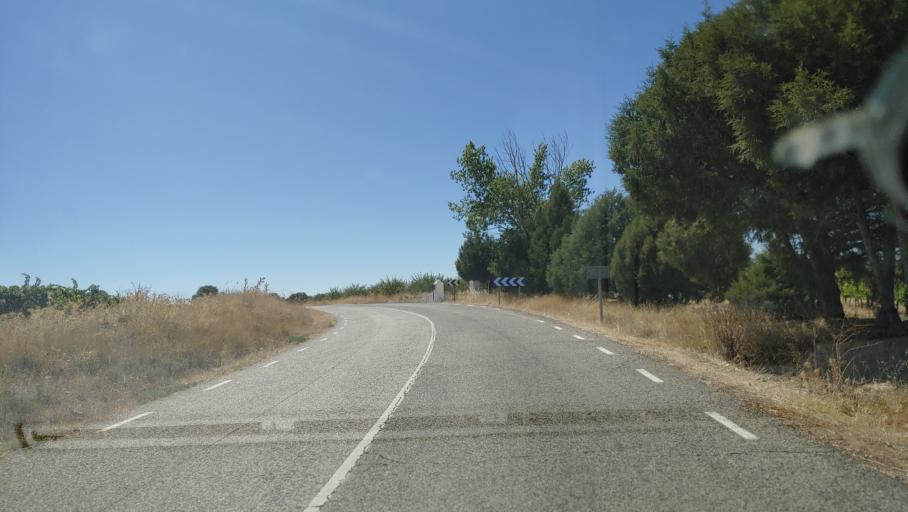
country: ES
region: Castille-La Mancha
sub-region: Provincia de Albacete
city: Ossa de Montiel
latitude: 38.8956
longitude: -2.7678
